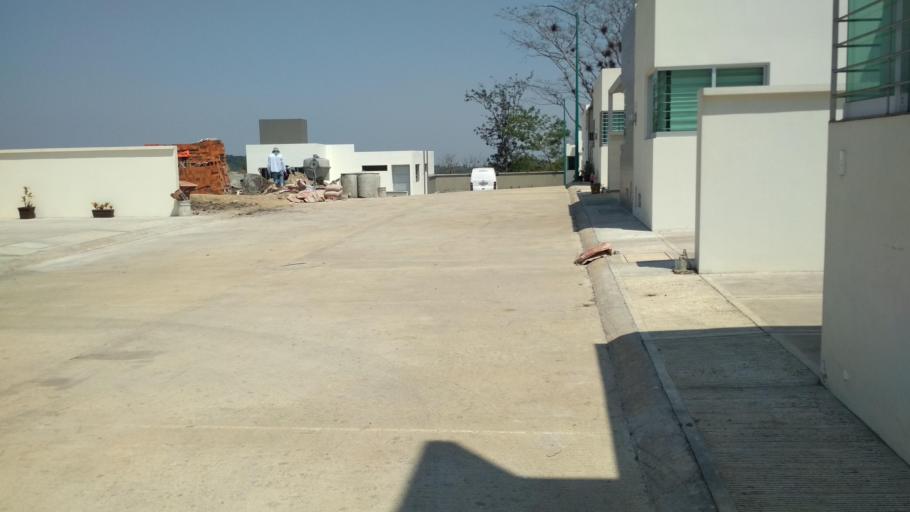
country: MX
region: Veracruz
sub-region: Emiliano Zapata
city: Las Trancas
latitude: 19.5158
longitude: -96.8481
